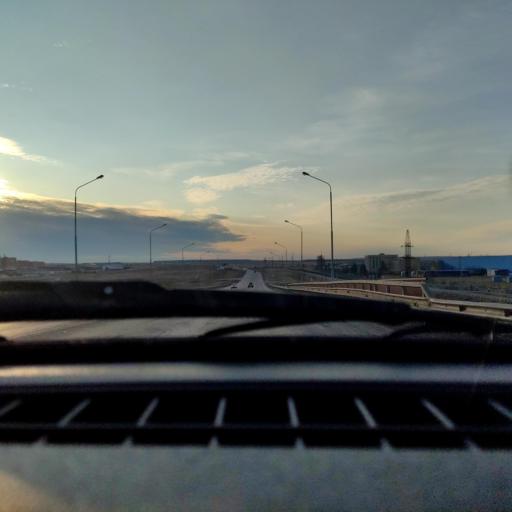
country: RU
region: Bashkortostan
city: Iglino
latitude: 54.7727
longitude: 56.2577
